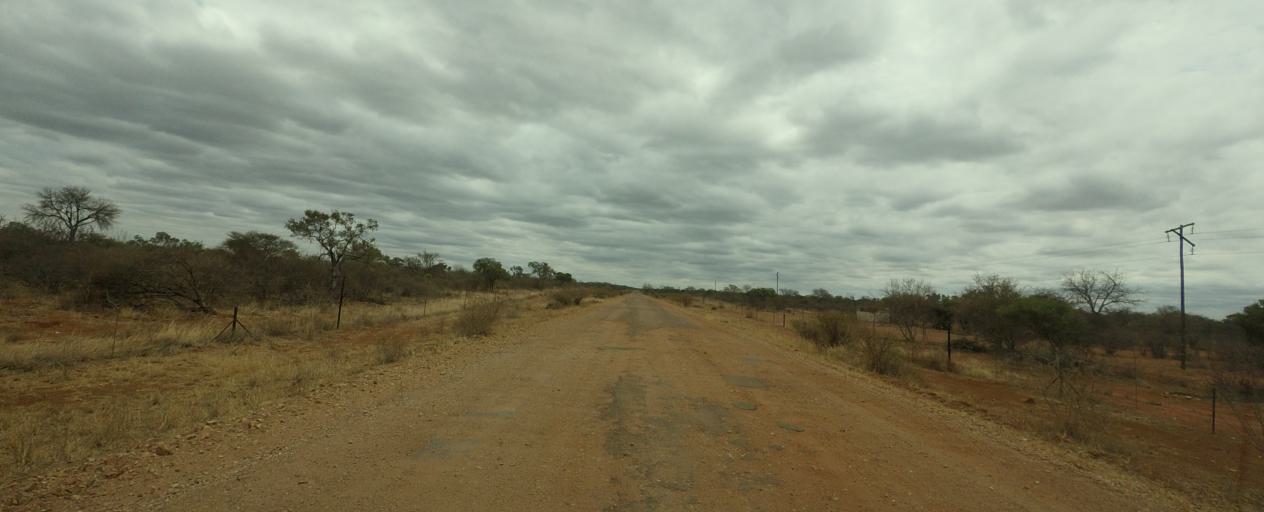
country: BW
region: Central
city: Mathathane
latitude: -22.7395
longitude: 28.4744
